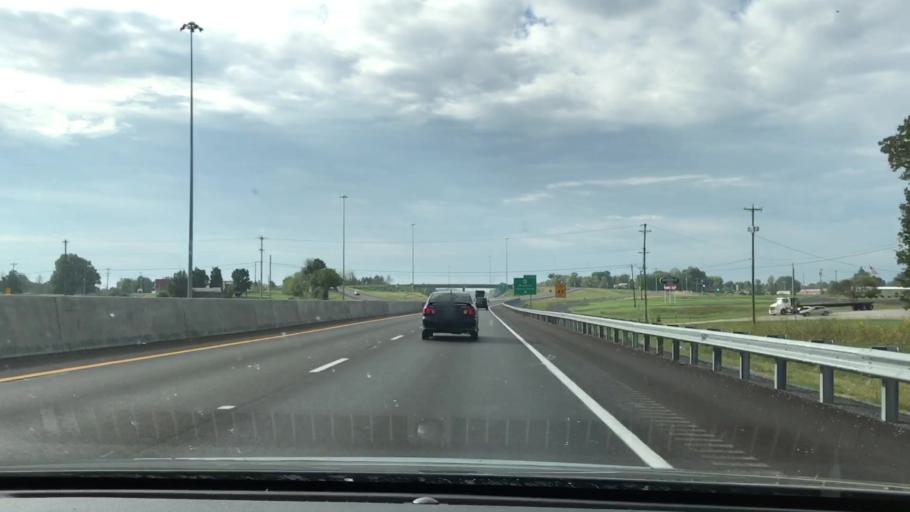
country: US
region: Kentucky
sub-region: Graves County
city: Mayfield
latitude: 36.7438
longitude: -88.6677
